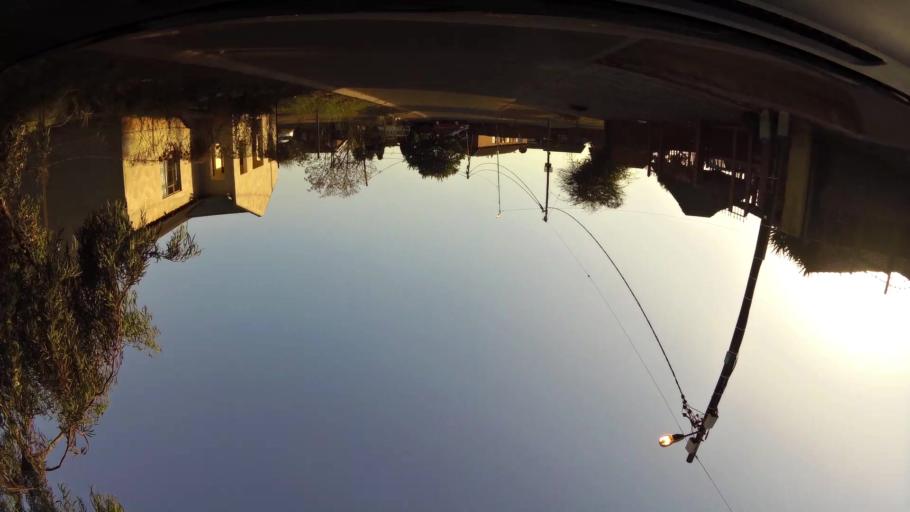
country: ZA
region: Gauteng
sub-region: City of Tshwane Metropolitan Municipality
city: Mabopane
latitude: -25.5826
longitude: 28.1026
